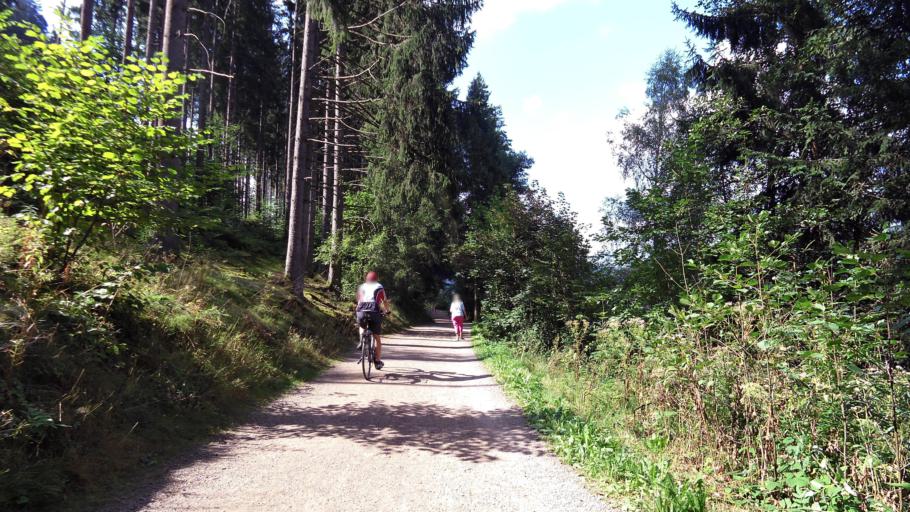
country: DE
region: Baden-Wuerttemberg
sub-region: Freiburg Region
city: Hinterzarten
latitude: 47.8921
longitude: 8.1505
